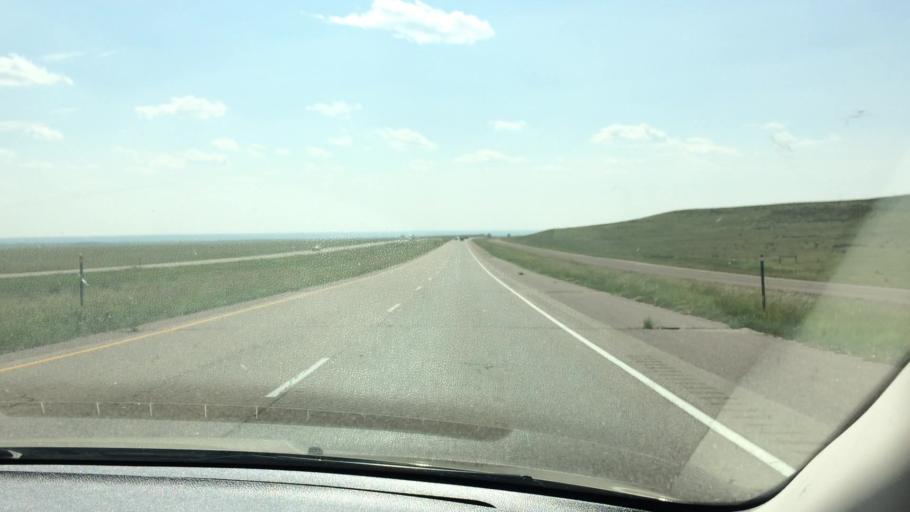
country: US
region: Colorado
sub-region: Lincoln County
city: Hugo
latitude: 39.2715
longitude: -103.5132
